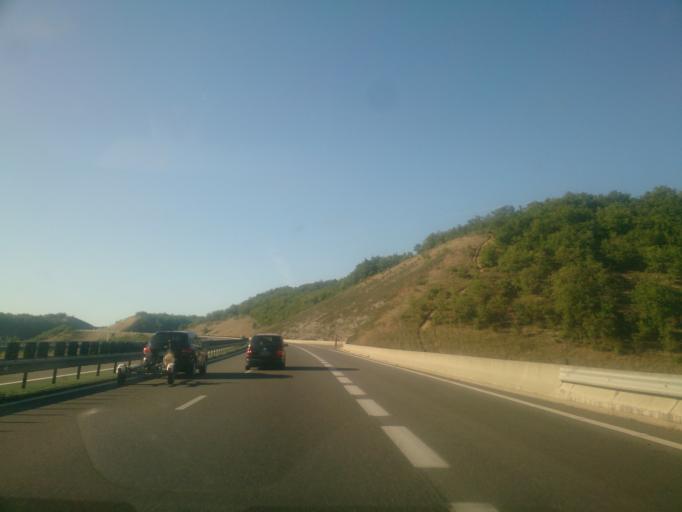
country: FR
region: Midi-Pyrenees
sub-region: Departement du Lot
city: Cahors
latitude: 44.4776
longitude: 1.5049
